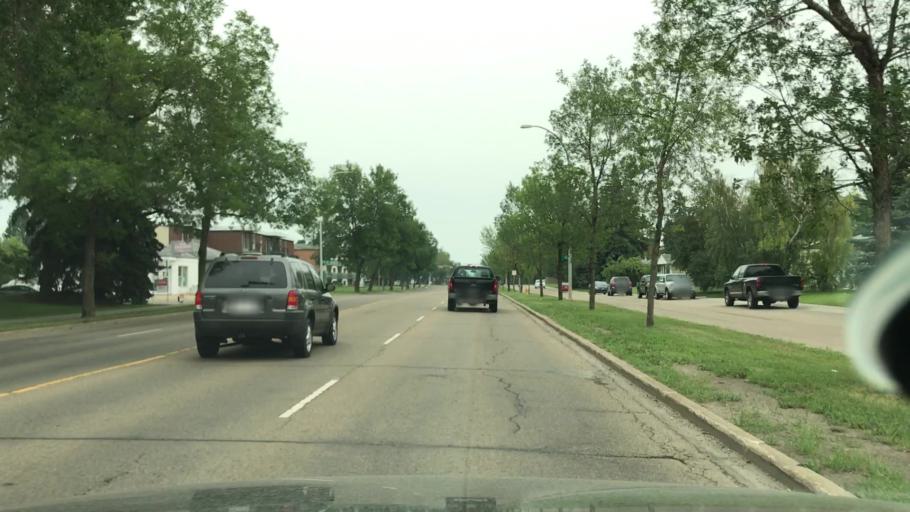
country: CA
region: Alberta
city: Edmonton
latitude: 53.5261
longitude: -113.5779
